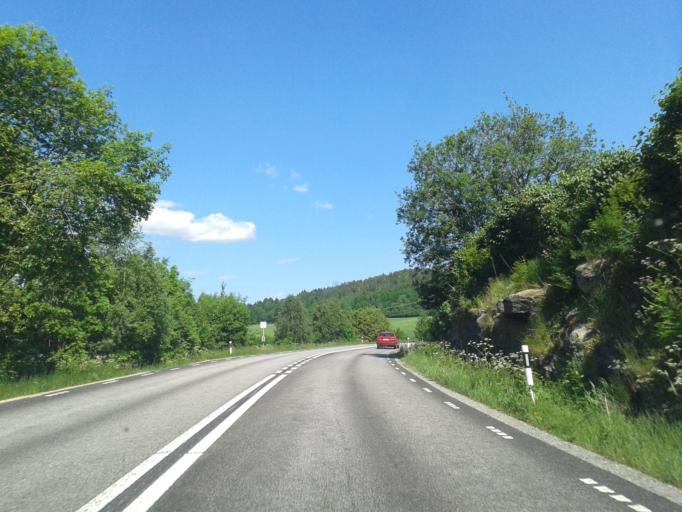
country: SE
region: Vaestra Goetaland
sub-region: Orust
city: Henan
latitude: 58.3209
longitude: 11.6789
